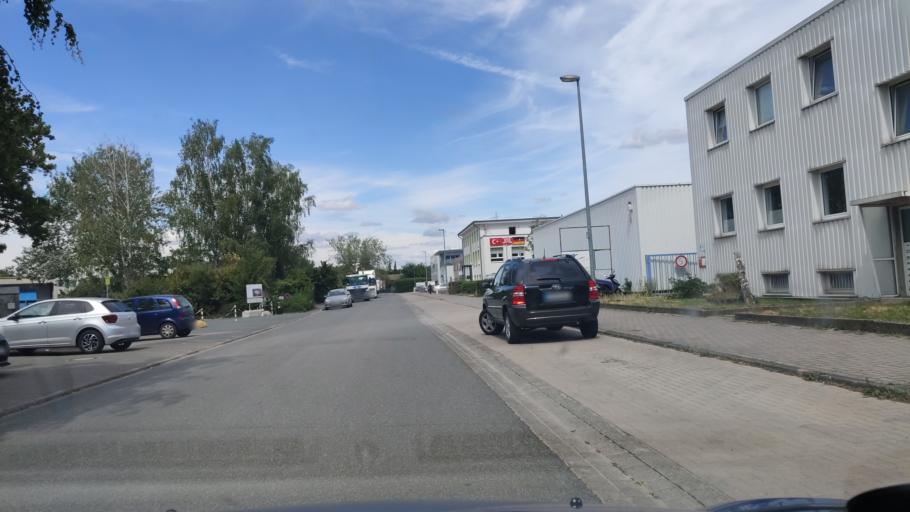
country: DE
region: Lower Saxony
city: Ronnenberg
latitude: 52.3452
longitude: 9.6728
